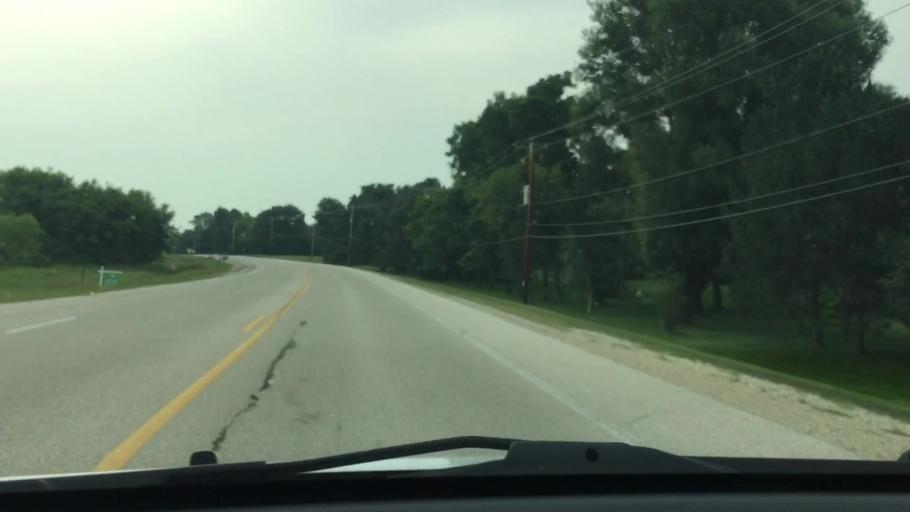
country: US
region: Wisconsin
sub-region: Waukesha County
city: New Berlin
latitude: 42.9914
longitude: -88.1599
